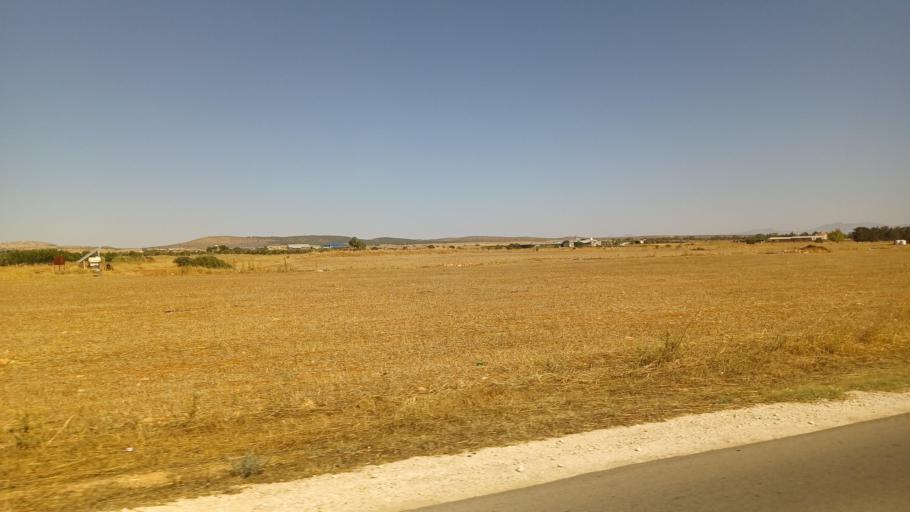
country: CY
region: Larnaka
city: Pergamos
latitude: 35.0286
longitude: 33.7050
